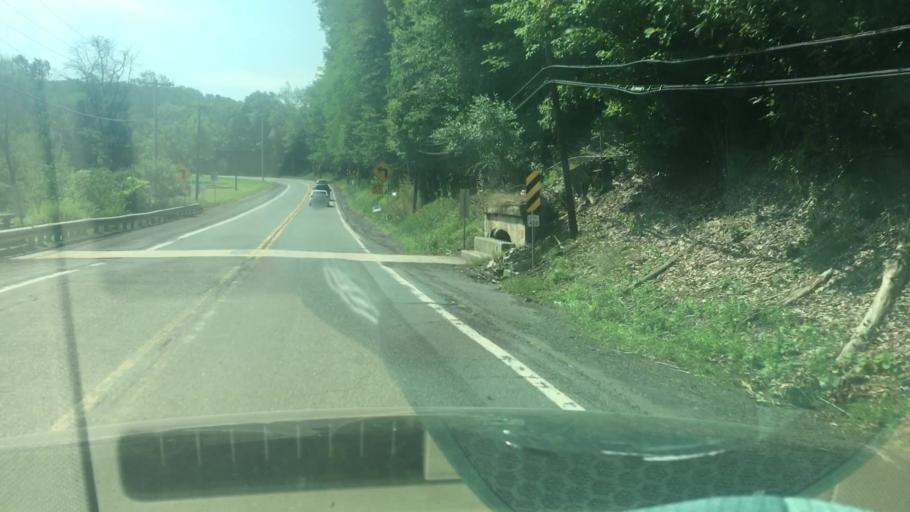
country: US
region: Pennsylvania
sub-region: Schuylkill County
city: Hometown
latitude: 40.8143
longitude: -76.0459
